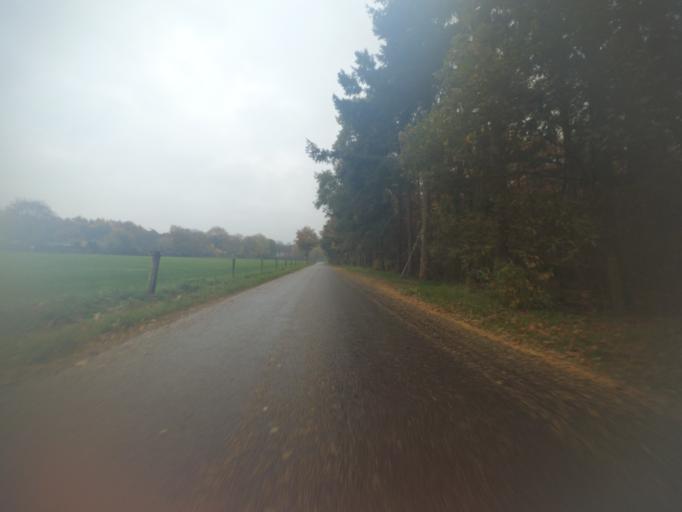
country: NL
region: Gelderland
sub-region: Gemeente Ede
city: Lunteren
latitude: 52.1064
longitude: 5.6428
